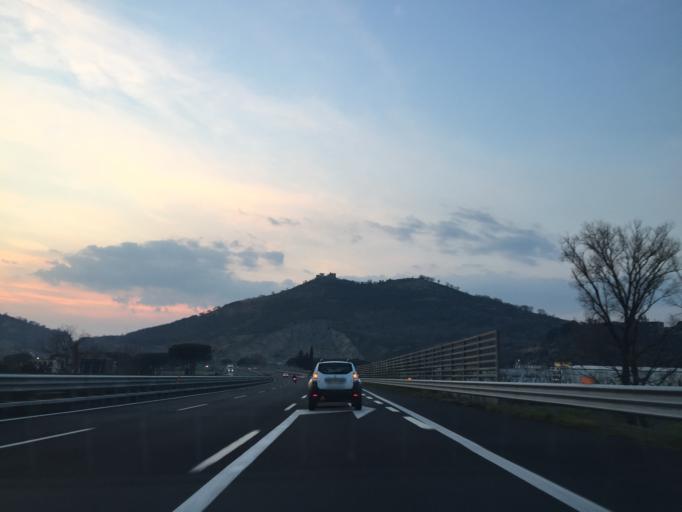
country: IT
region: Campania
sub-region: Provincia di Salerno
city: Lanzara
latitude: 40.7698
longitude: 14.6718
